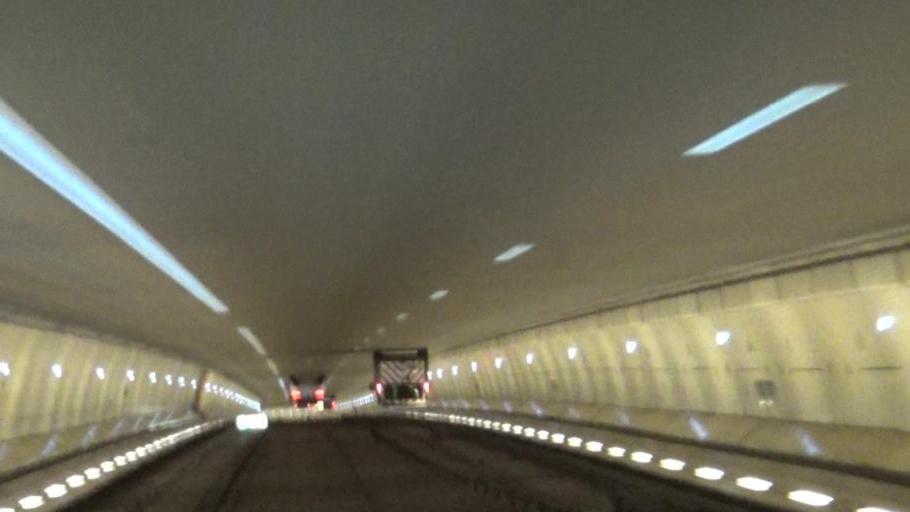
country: FR
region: Ile-de-France
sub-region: Departement des Yvelines
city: Bougival
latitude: 48.8673
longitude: 2.1595
